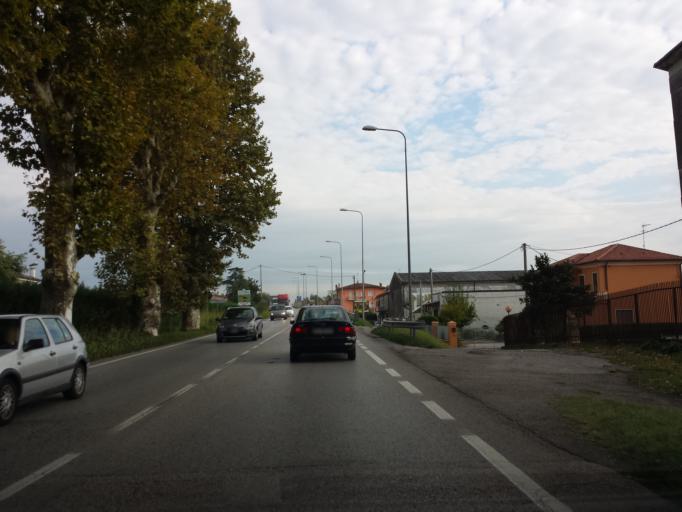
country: IT
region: Veneto
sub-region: Provincia di Padova
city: Boara Pisani
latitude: 45.1080
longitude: 11.7813
